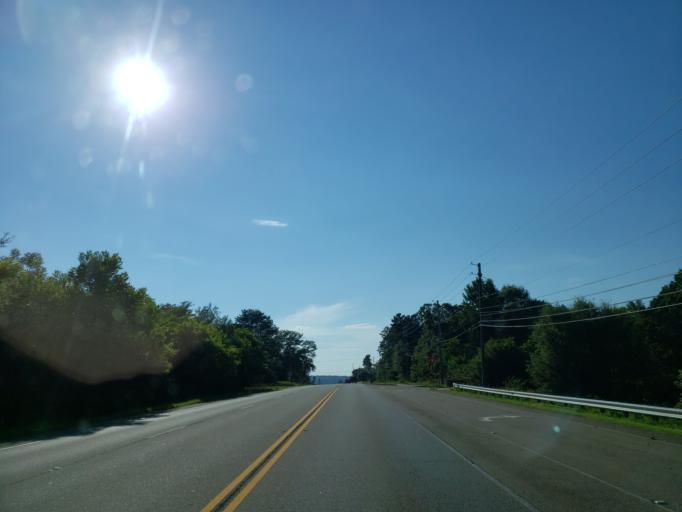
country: US
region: Georgia
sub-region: Cherokee County
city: Ball Ground
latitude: 34.2530
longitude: -84.3132
